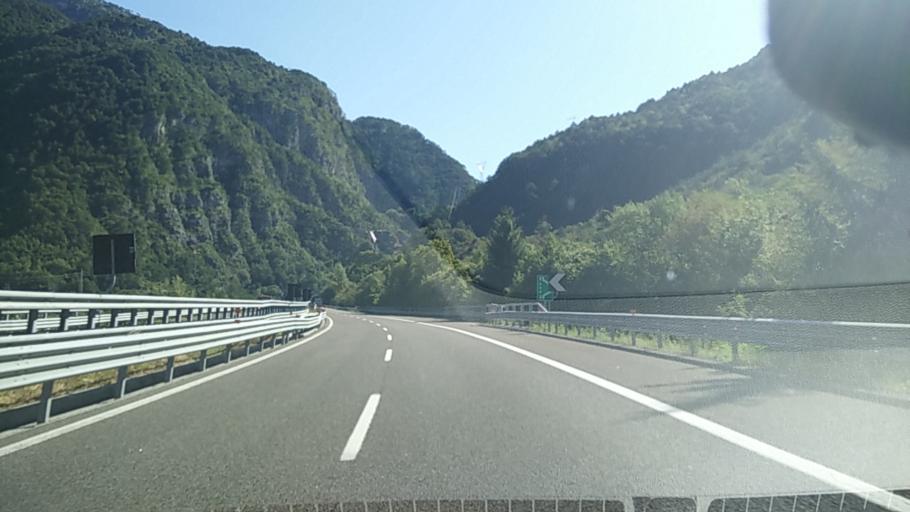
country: IT
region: Friuli Venezia Giulia
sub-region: Provincia di Udine
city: Resiutta
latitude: 46.3943
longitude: 13.2590
